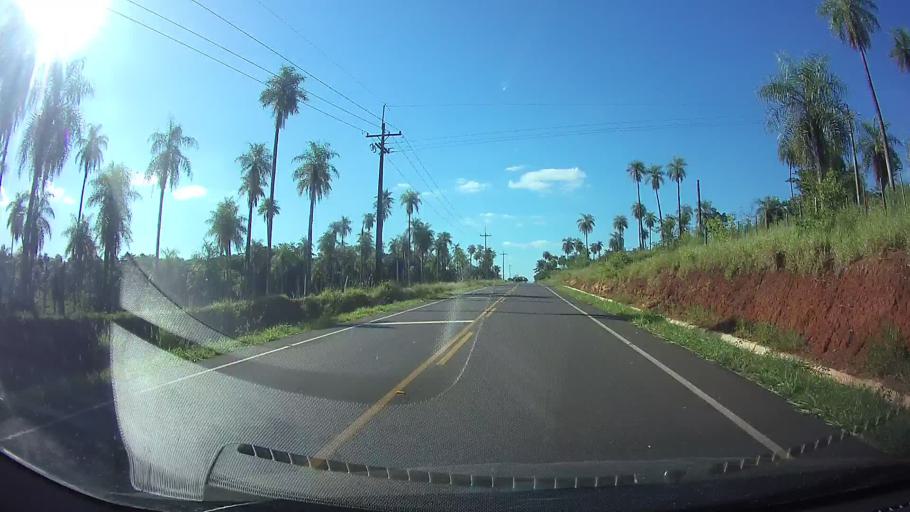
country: PY
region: Cordillera
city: Caacupe
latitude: -25.3343
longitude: -57.1562
